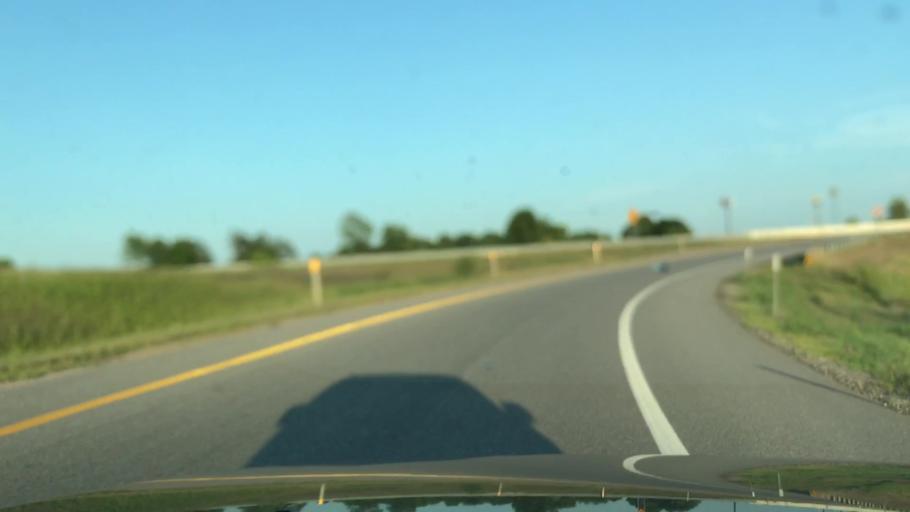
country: US
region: Michigan
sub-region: Osceola County
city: Reed City
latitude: 43.8910
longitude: -85.5291
